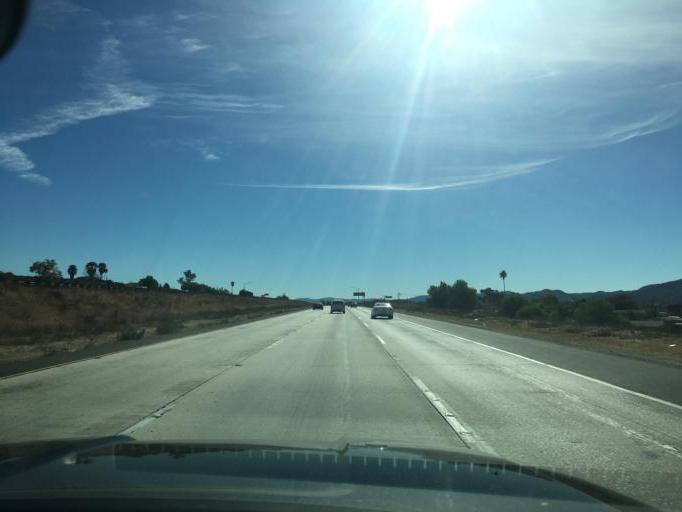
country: US
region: California
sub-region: Riverside County
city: Sedco Hills
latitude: 33.6336
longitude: -117.2782
